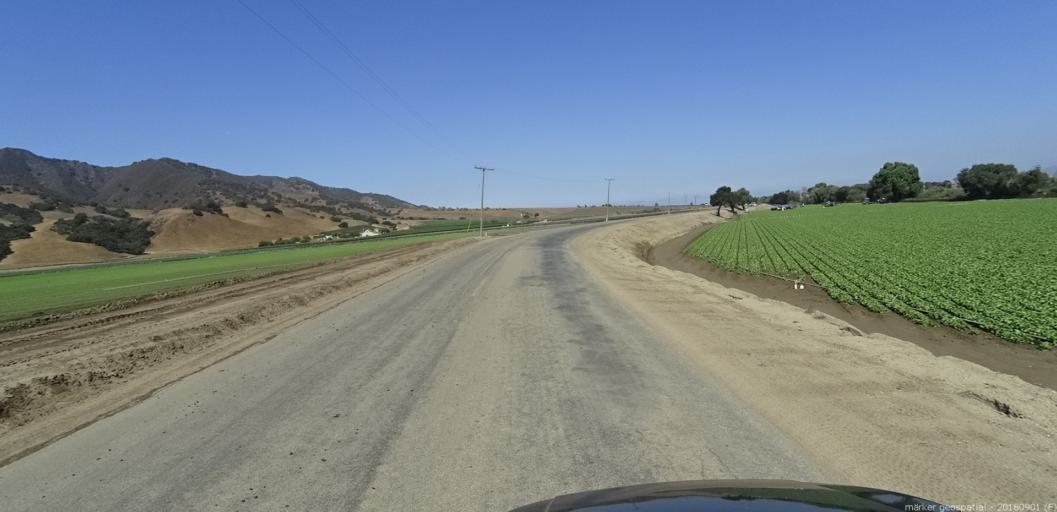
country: US
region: California
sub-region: Monterey County
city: Chualar
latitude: 36.5419
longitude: -121.5428
